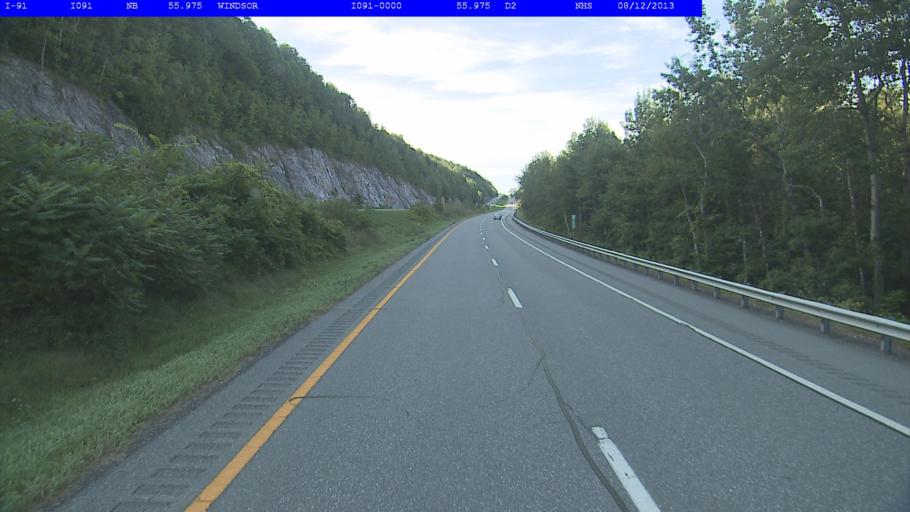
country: US
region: Vermont
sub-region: Windsor County
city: Windsor
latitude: 43.4656
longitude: -72.4059
